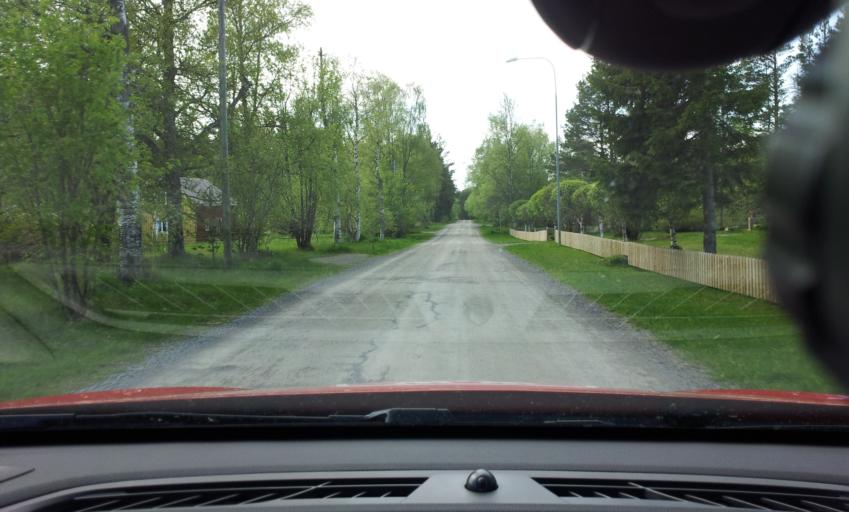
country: SE
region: Jaemtland
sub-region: Bergs Kommun
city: Hoverberg
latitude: 62.9399
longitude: 14.5173
